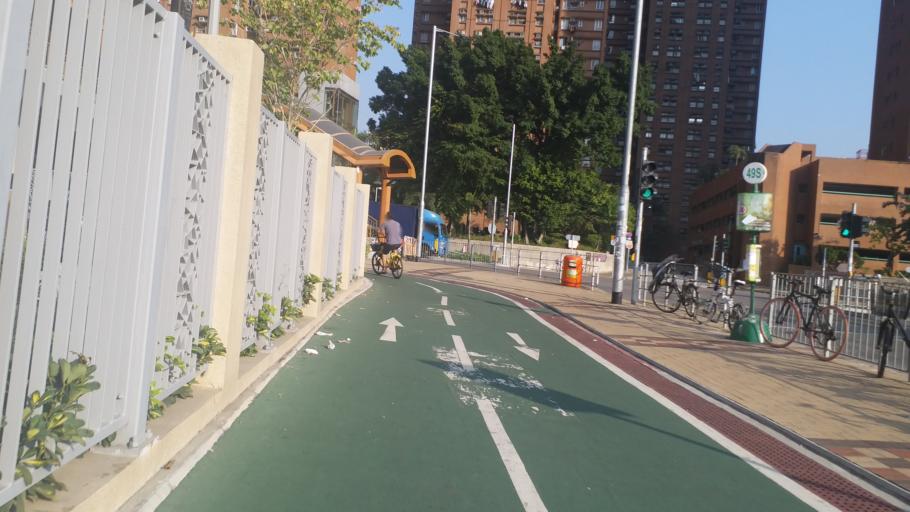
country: HK
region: Tuen Mun
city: Tuen Mun
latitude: 22.4135
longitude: 113.9763
